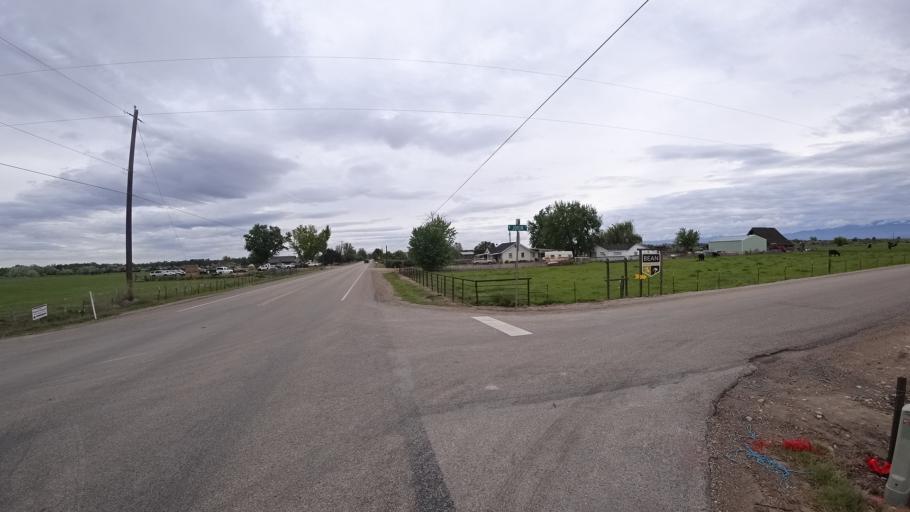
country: US
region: Idaho
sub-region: Ada County
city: Star
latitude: 43.6703
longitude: -116.4933
